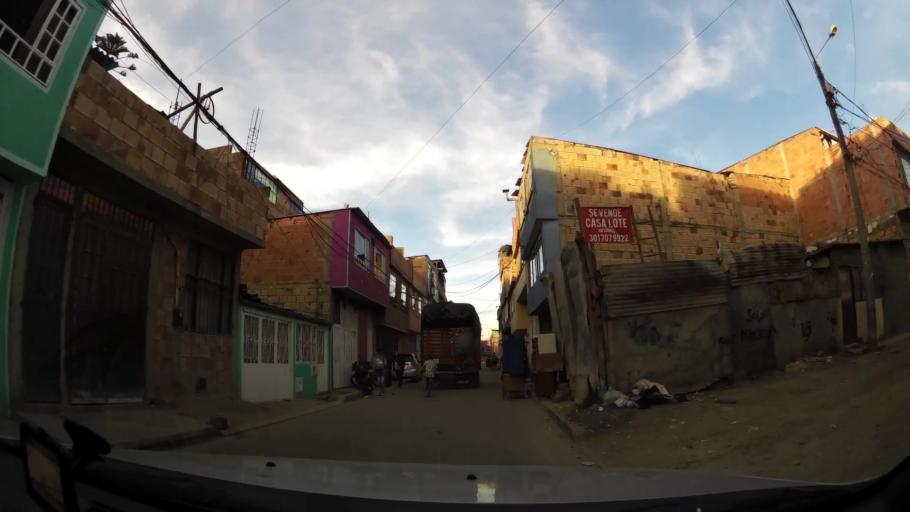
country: CO
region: Cundinamarca
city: Soacha
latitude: 4.6303
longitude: -74.1654
